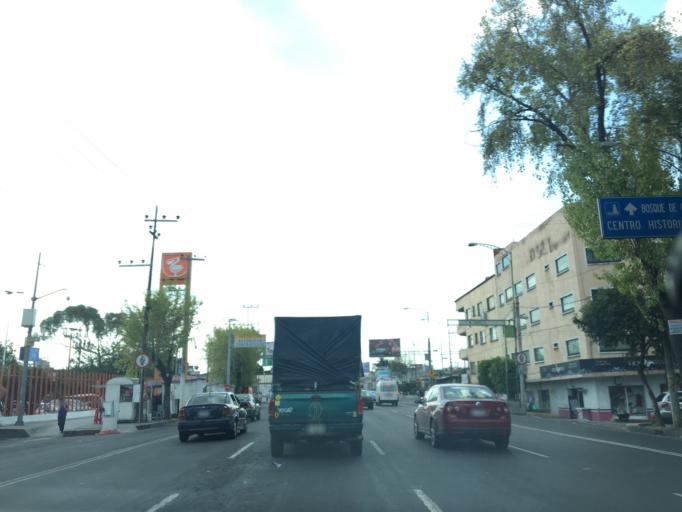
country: MX
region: Mexico City
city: Mexico City
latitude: 19.4086
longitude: -99.1327
